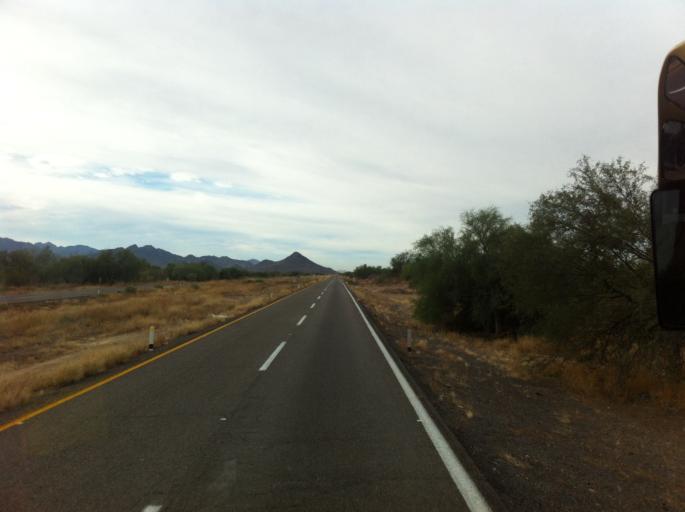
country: MX
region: Sonora
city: Hermosillo
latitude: 28.6956
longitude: -110.9886
